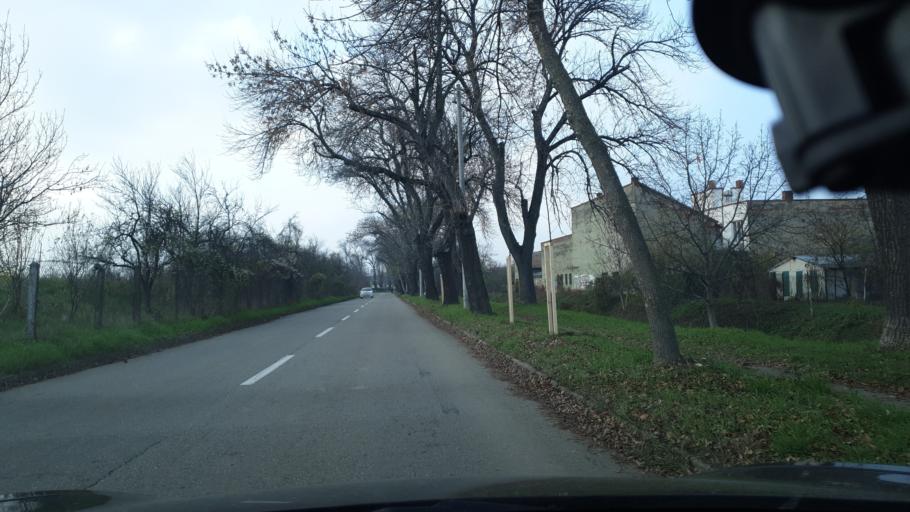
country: RO
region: Timis
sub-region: Comuna Ghiroda
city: Ghiroda
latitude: 45.7592
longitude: 21.2687
